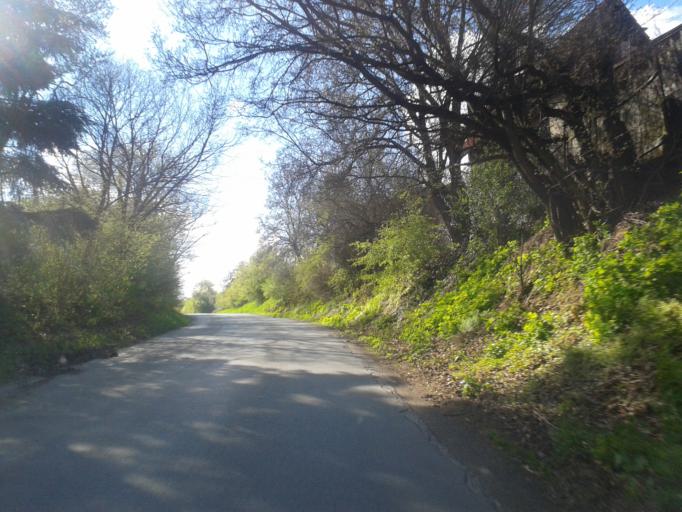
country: CZ
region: Central Bohemia
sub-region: Okres Beroun
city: Lodenice
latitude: 50.0108
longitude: 14.1456
